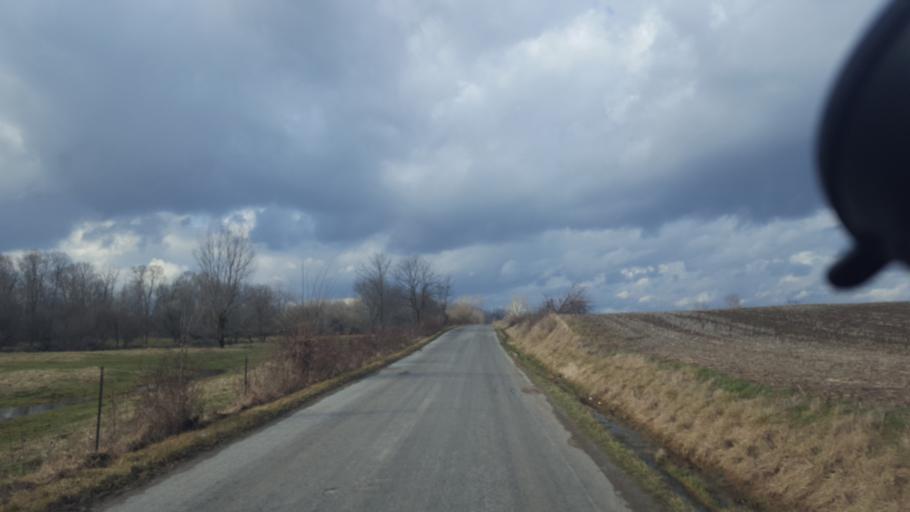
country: US
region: Ohio
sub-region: Knox County
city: Fredericktown
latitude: 40.5280
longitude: -82.5933
